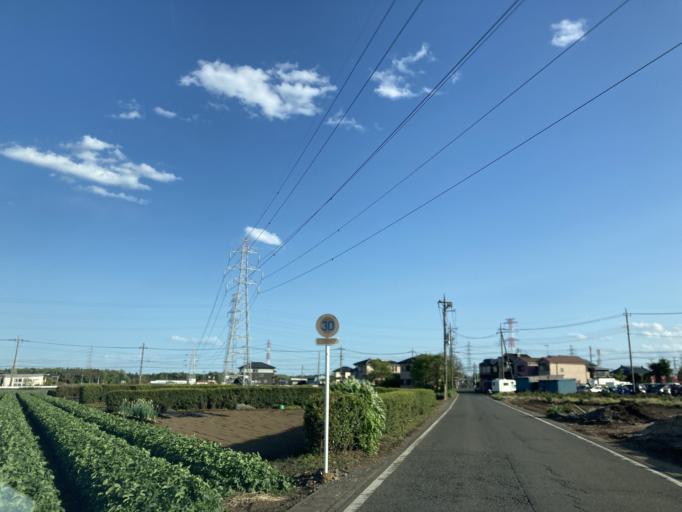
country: JP
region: Saitama
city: Sayama
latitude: 35.8511
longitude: 139.4453
